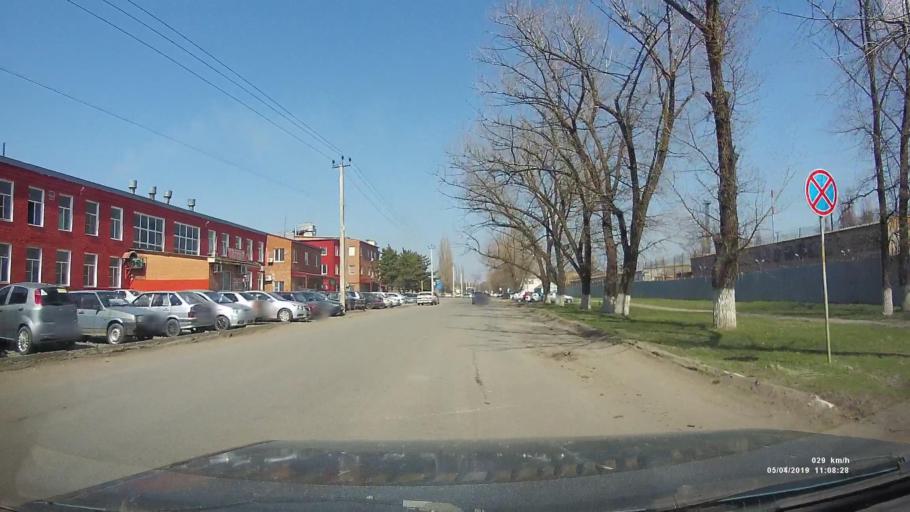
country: RU
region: Rostov
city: Azov
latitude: 47.0859
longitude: 39.4354
